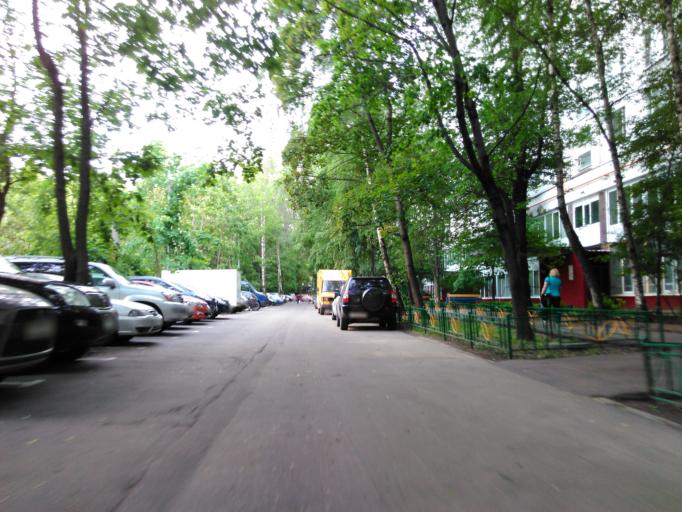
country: RU
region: Moscow
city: Ramenki
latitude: 55.6737
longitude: 37.5165
